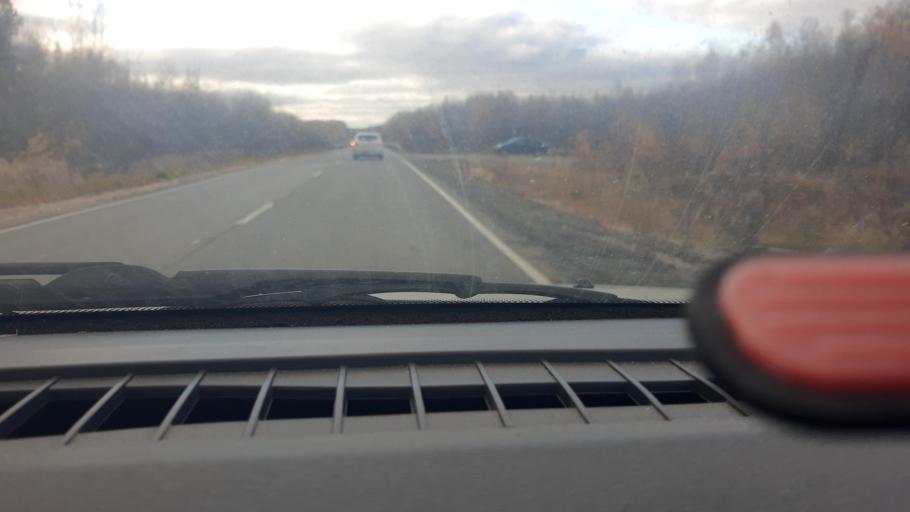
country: RU
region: Nizjnij Novgorod
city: Babino
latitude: 56.2969
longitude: 43.6184
